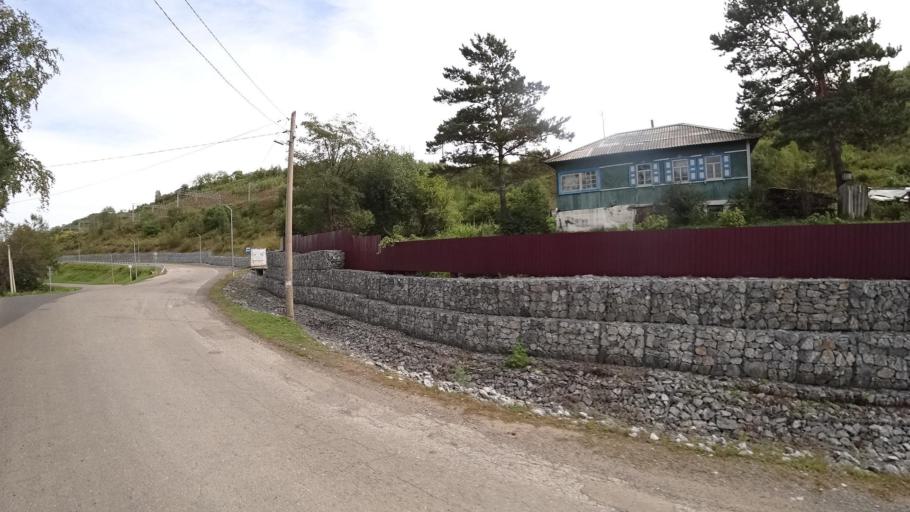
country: RU
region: Jewish Autonomous Oblast
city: Khingansk
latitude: 48.9961
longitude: 131.0565
